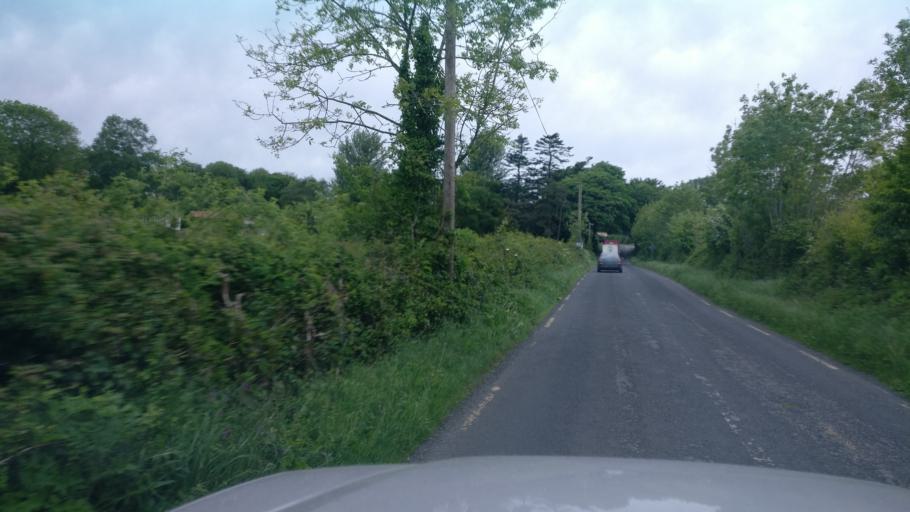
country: IE
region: Connaught
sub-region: County Galway
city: Portumna
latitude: 53.1184
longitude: -8.3120
